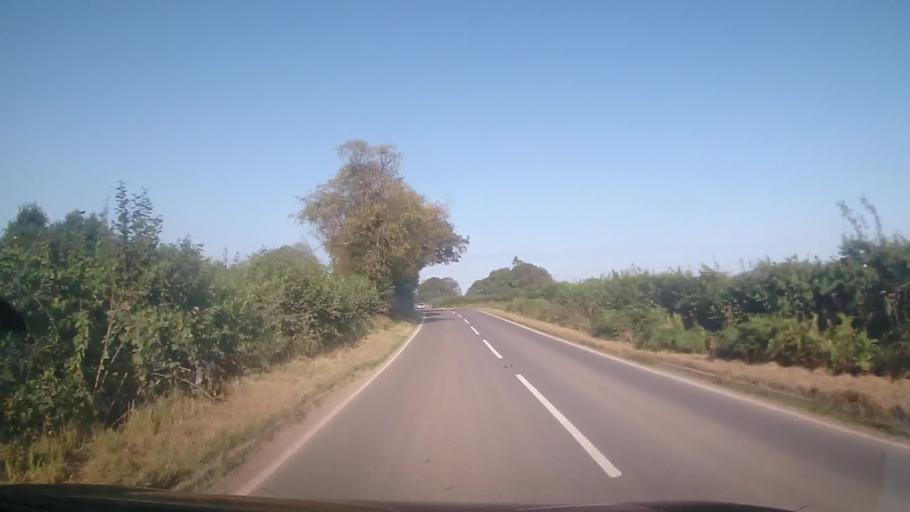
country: GB
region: Wales
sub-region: County of Ceredigion
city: Llangybi
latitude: 52.1863
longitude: -3.9979
